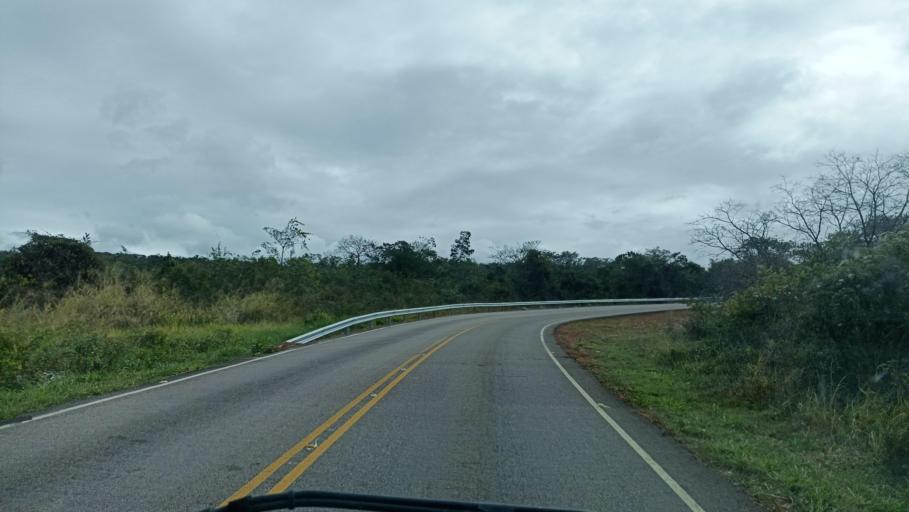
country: BR
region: Bahia
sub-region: Andarai
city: Vera Cruz
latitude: -12.9333
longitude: -41.2409
